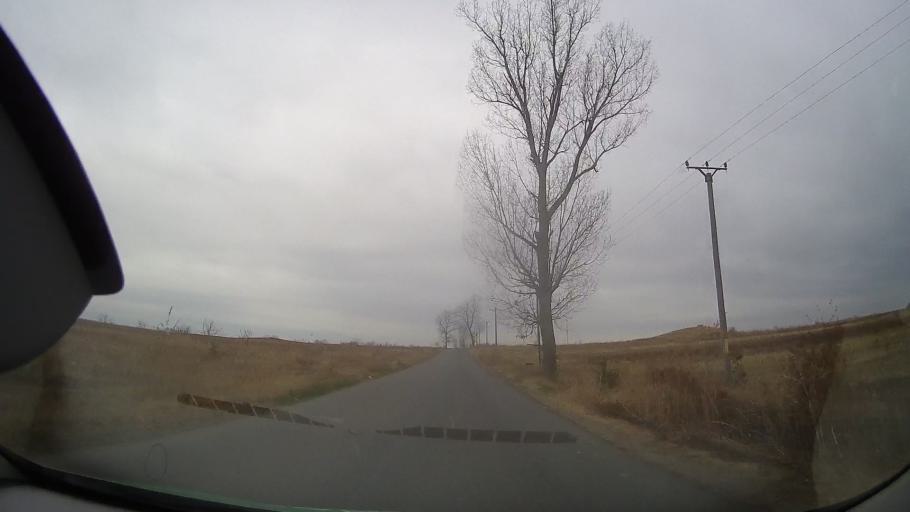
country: RO
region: Braila
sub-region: Comuna Ciresu
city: Ciresu
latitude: 44.9402
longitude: 27.3924
